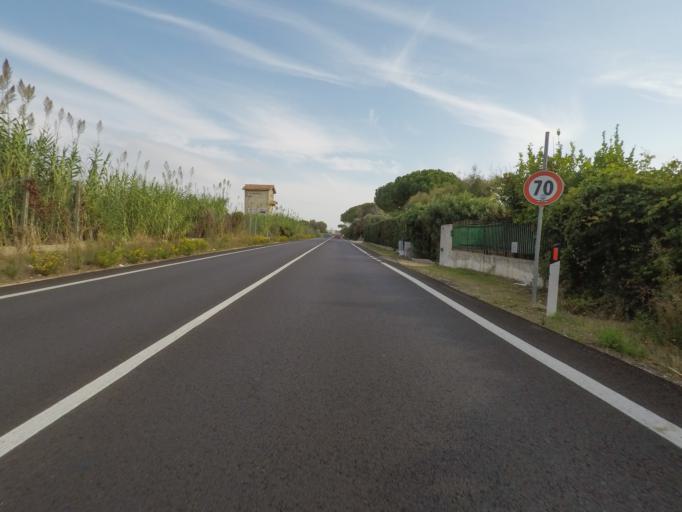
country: IT
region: Latium
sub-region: Citta metropolitana di Roma Capitale
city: Santa Marinella
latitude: 42.0478
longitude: 11.8218
